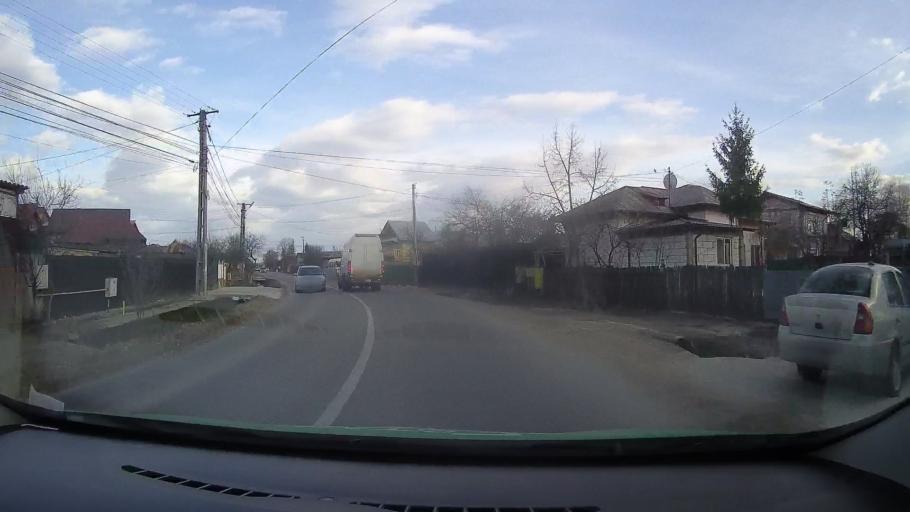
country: RO
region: Dambovita
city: Razvad
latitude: 44.9322
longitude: 25.5466
